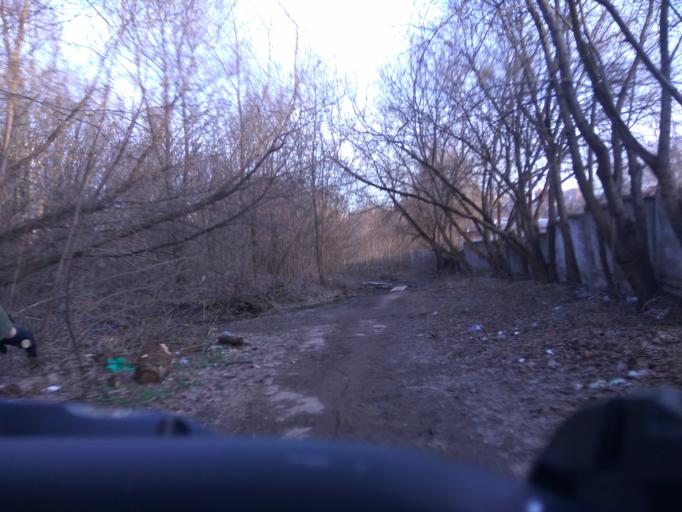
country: RU
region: Moscow
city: Vorob'yovo
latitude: 55.7285
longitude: 37.5169
